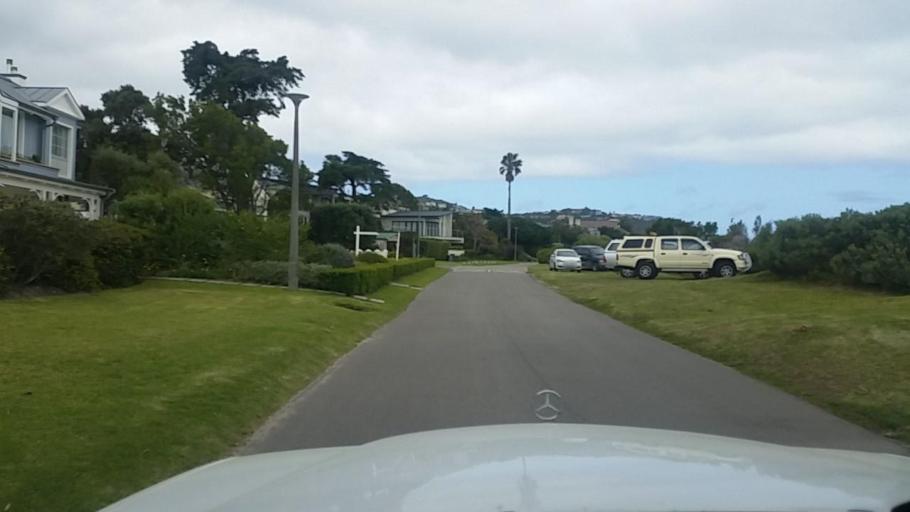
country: ZA
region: Western Cape
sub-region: Eden District Municipality
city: Knysna
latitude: -34.0653
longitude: 23.0550
